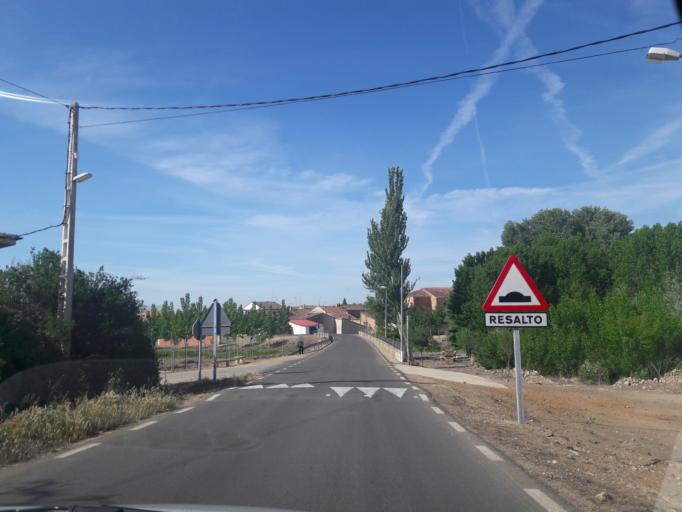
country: ES
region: Castille and Leon
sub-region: Provincia de Salamanca
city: Espino de la Orbada
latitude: 41.1094
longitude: -5.4227
